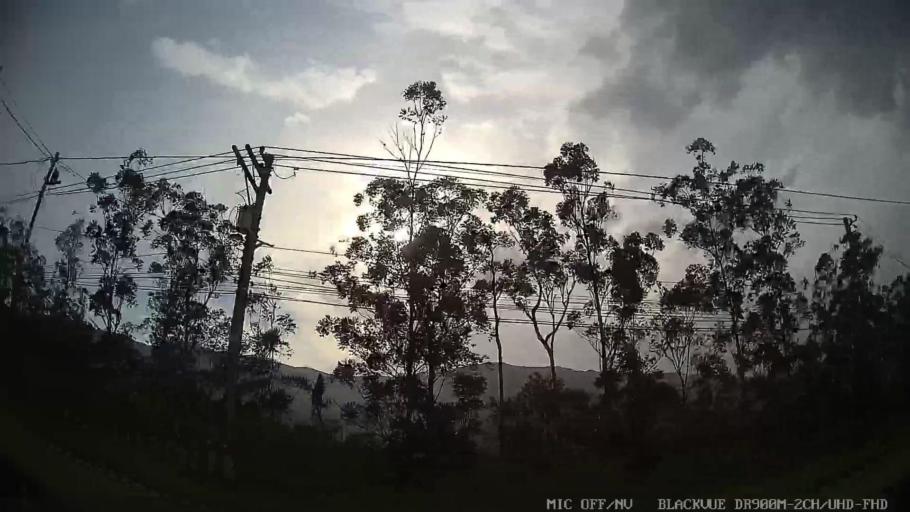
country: BR
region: Sao Paulo
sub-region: Cubatao
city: Cubatao
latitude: -23.8751
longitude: -46.4250
